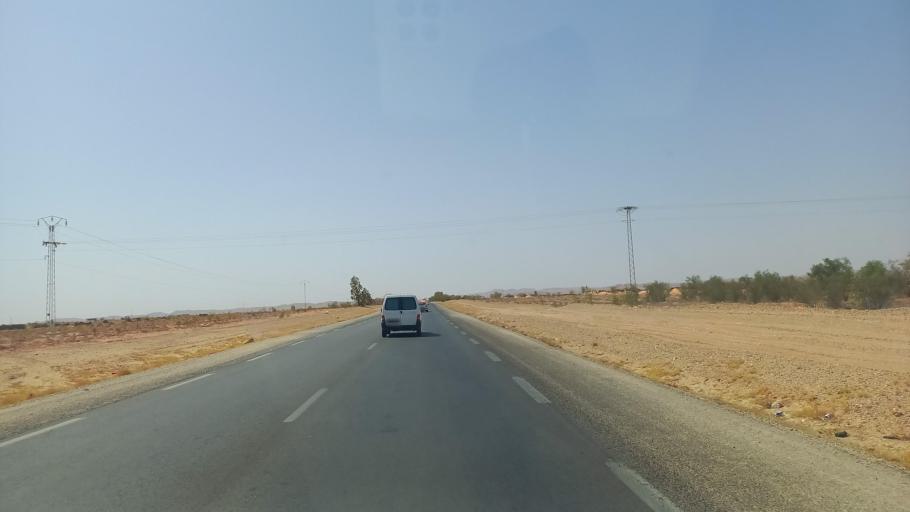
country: TN
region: Madanin
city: Medenine
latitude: 33.2200
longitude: 10.4494
